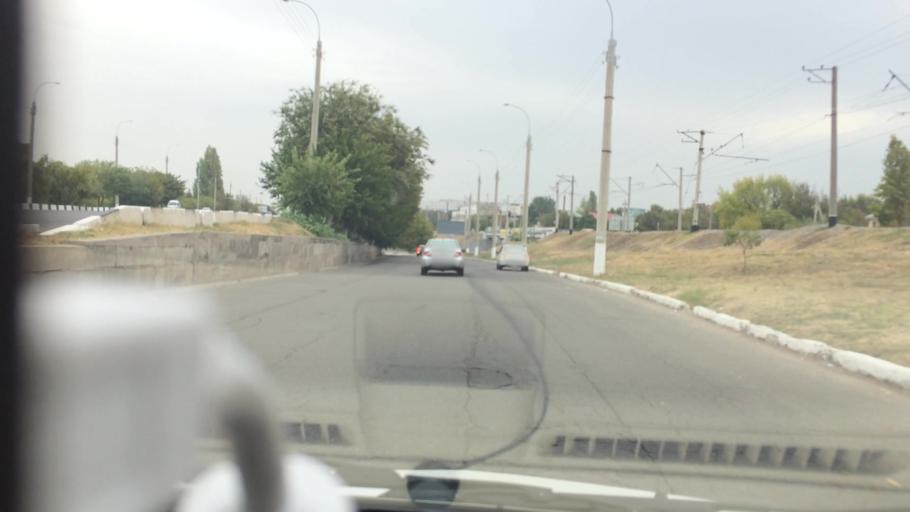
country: UZ
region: Toshkent
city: Salor
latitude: 41.3170
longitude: 69.3110
